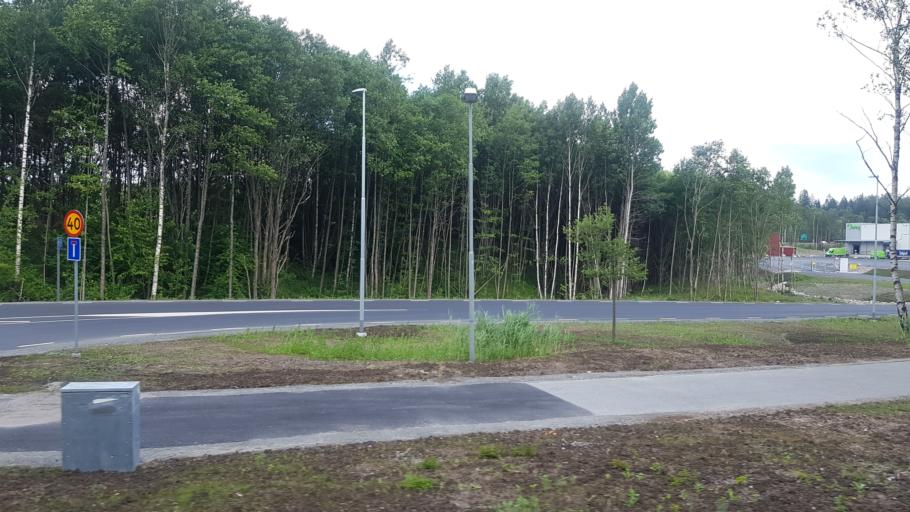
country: SE
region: Vaestra Goetaland
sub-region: Harryda Kommun
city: Molnlycke
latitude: 57.6675
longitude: 12.1028
